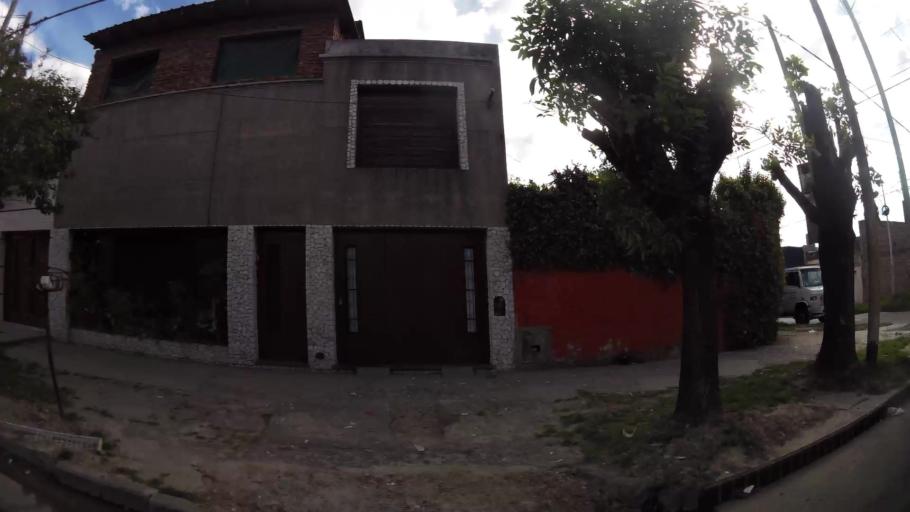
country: AR
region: Buenos Aires
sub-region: Partido de Avellaneda
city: Avellaneda
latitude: -34.6929
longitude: -58.3633
